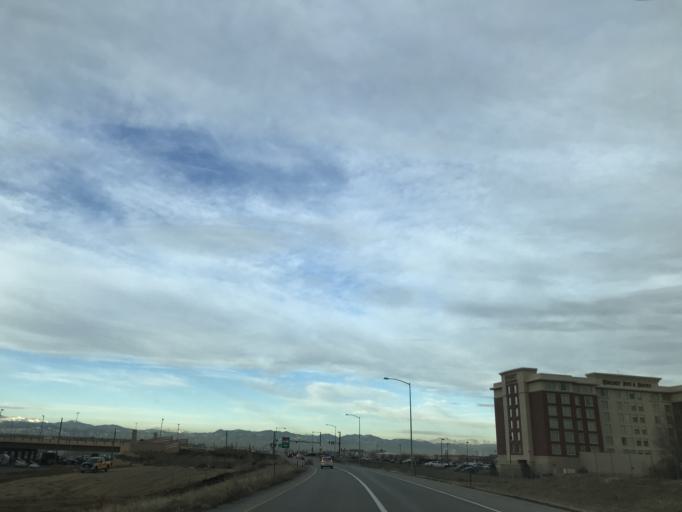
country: US
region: Colorado
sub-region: Adams County
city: Commerce City
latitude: 39.7777
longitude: -104.8796
